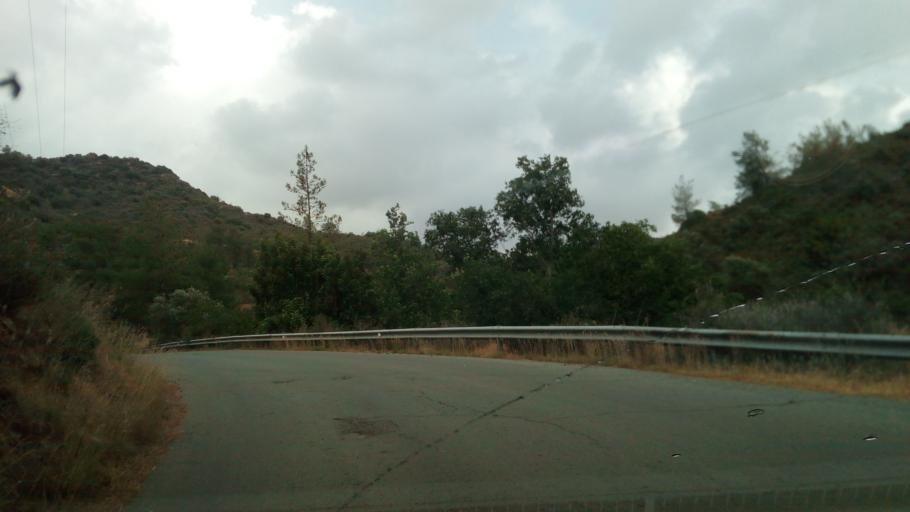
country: CY
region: Limassol
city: Parekklisha
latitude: 34.8507
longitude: 33.1875
